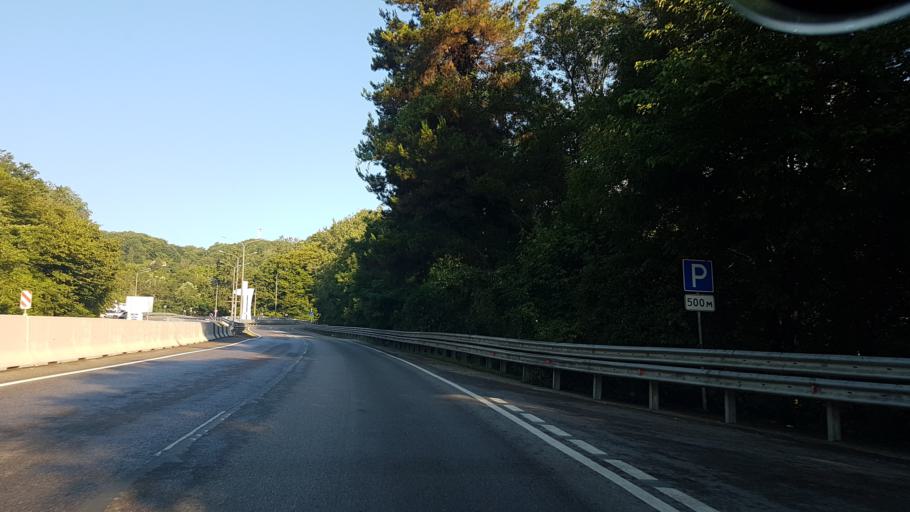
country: RU
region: Krasnodarskiy
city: Dagomys
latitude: 43.6443
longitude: 39.6982
